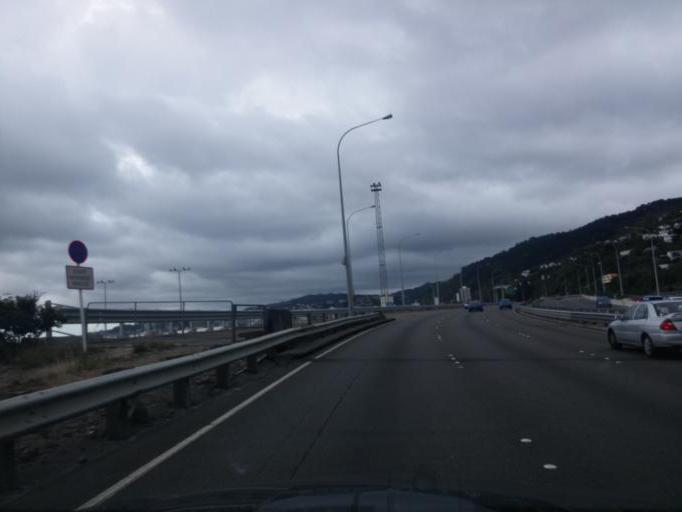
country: NZ
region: Wellington
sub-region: Wellington City
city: Wellington
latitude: -41.2612
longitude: 174.7911
